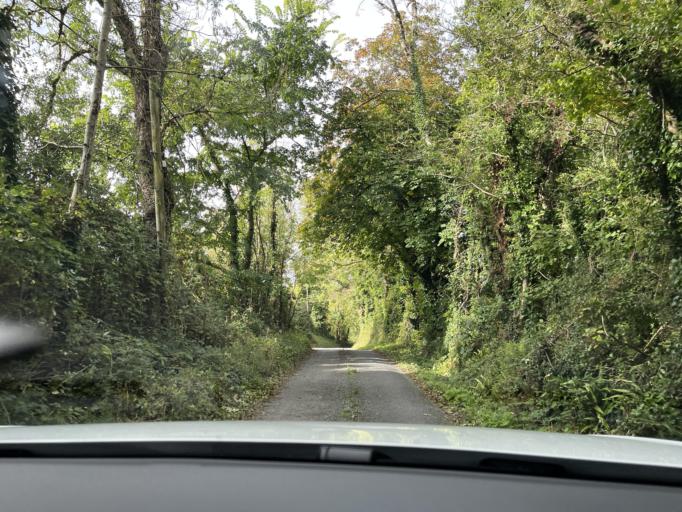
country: IE
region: Connaught
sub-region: County Leitrim
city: Carrick-on-Shannon
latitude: 53.9627
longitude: -8.0726
